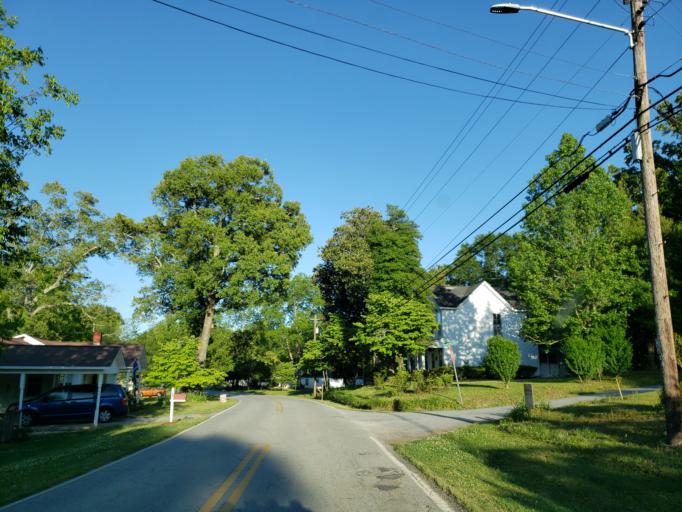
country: US
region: Georgia
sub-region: Haralson County
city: Tallapoosa
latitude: 33.7543
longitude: -85.3016
